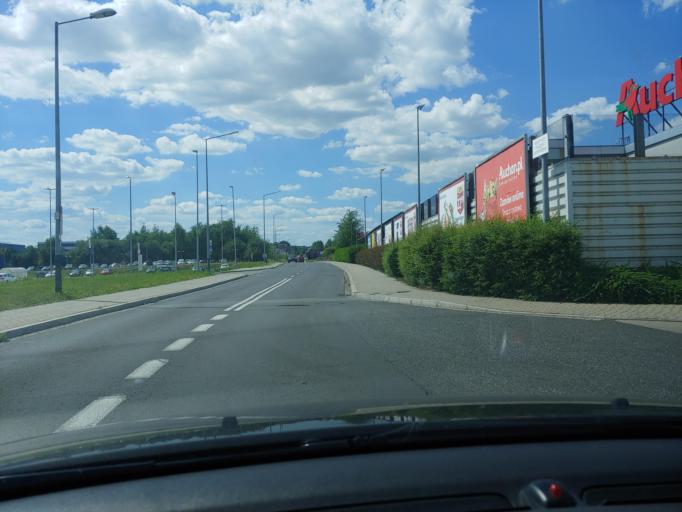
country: PL
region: Lesser Poland Voivodeship
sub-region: Powiat krakowski
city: Zielonki
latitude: 50.0907
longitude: 19.8998
